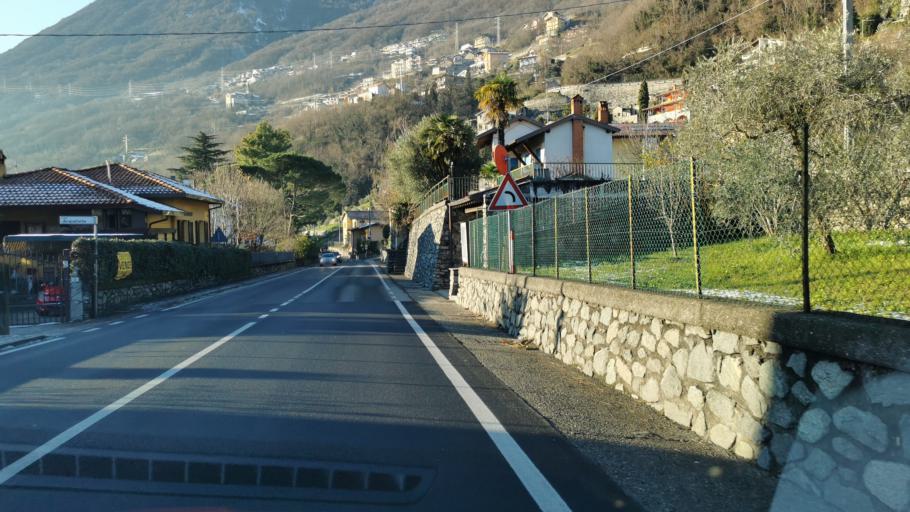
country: IT
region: Lombardy
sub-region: Provincia di Como
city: Gera Lario
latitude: 46.1695
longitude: 9.3653
